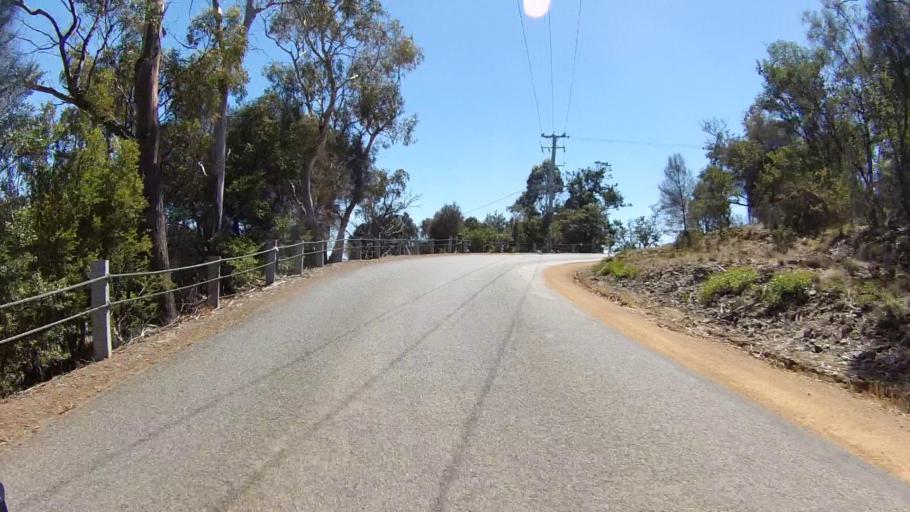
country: AU
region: Tasmania
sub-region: Clarence
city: Cambridge
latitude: -42.8541
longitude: 147.4232
